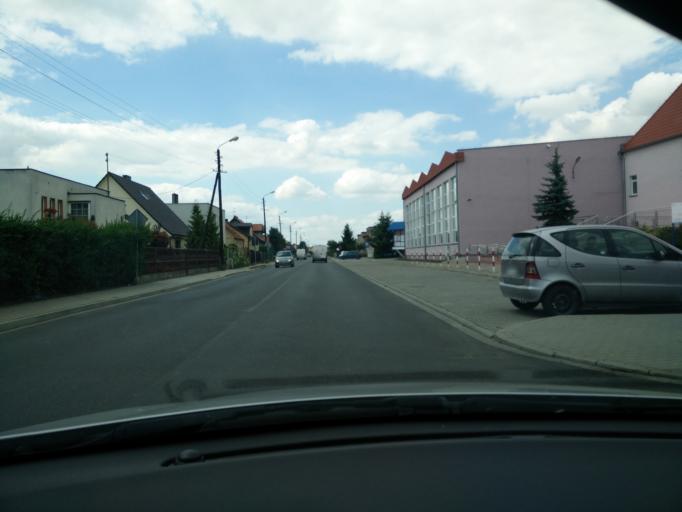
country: PL
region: Greater Poland Voivodeship
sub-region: Powiat sredzki
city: Sroda Wielkopolska
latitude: 52.2302
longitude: 17.2622
